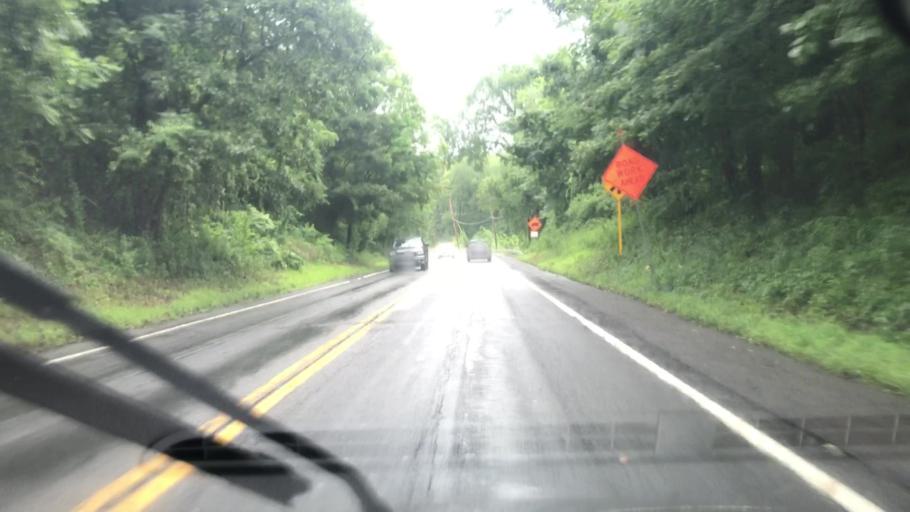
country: US
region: New York
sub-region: Westchester County
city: Jefferson Valley-Yorktown
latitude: 41.3373
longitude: -73.7733
